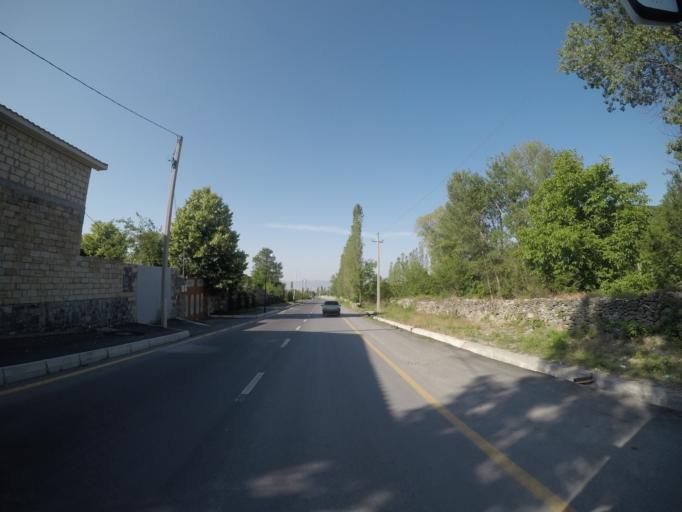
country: AZ
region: Shaki City
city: Sheki
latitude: 41.2237
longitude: 47.1718
